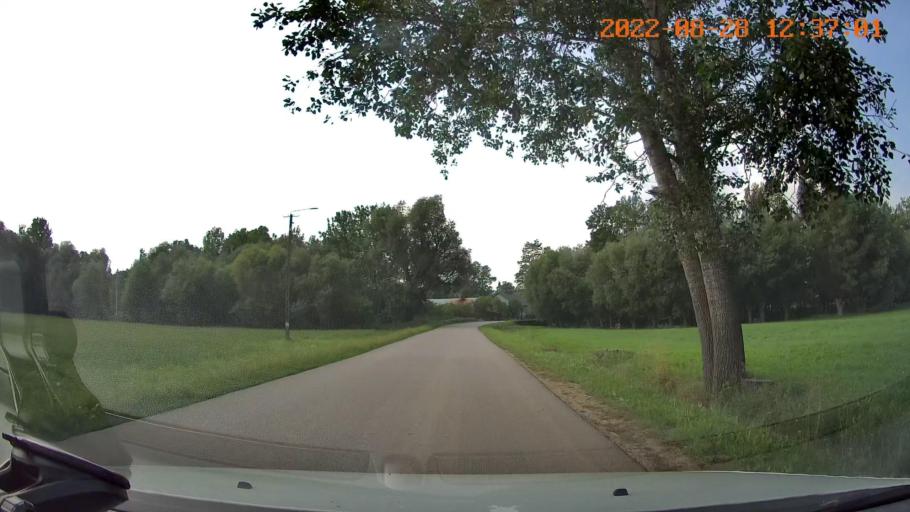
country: PL
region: Swietokrzyskie
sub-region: Powiat kazimierski
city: Skalbmierz
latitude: 50.3688
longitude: 20.4021
